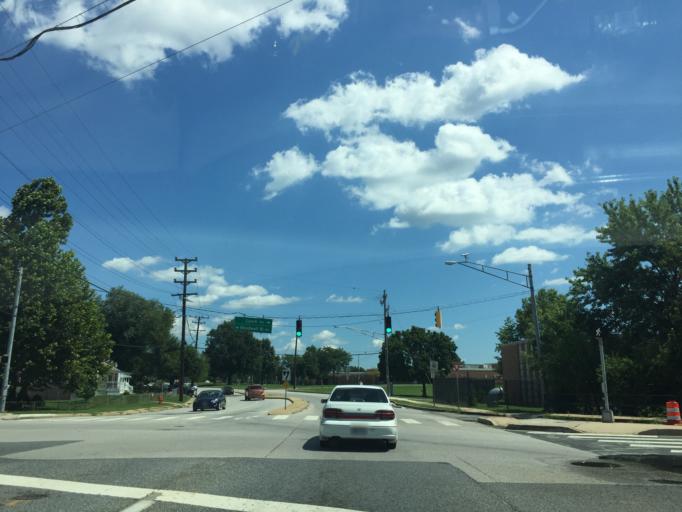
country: US
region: Maryland
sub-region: Baltimore County
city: Dundalk
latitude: 39.2730
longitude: -76.4943
